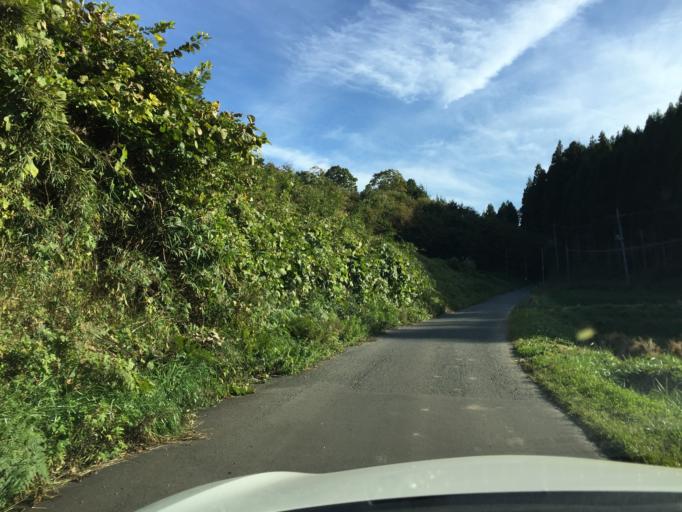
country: JP
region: Fukushima
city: Ishikawa
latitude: 37.2436
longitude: 140.6081
